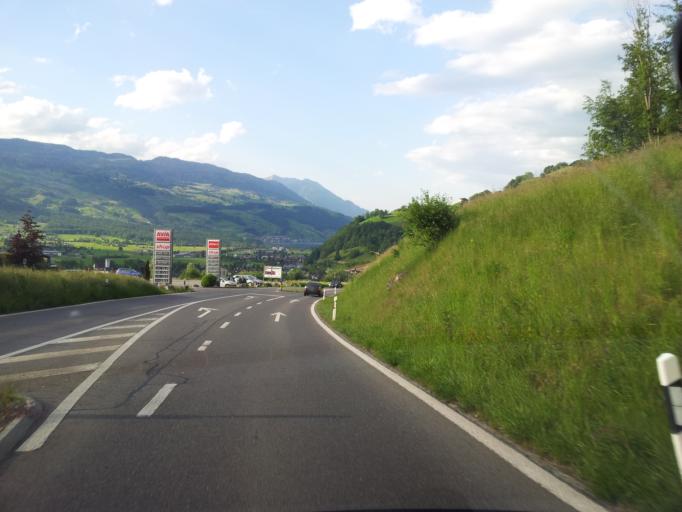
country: CH
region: Obwalden
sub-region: Obwalden
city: Giswil
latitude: 46.8201
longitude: 8.1784
